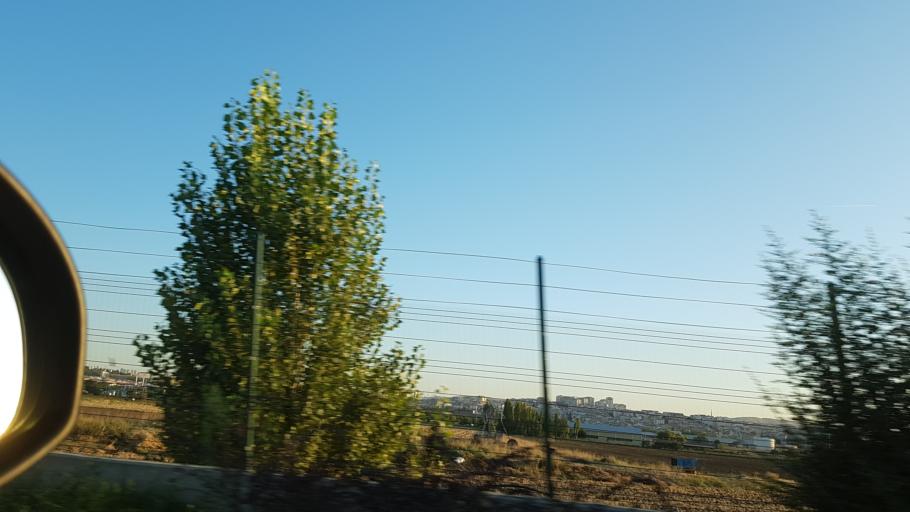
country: TR
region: Ankara
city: Etimesgut
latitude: 39.9627
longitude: 32.6571
